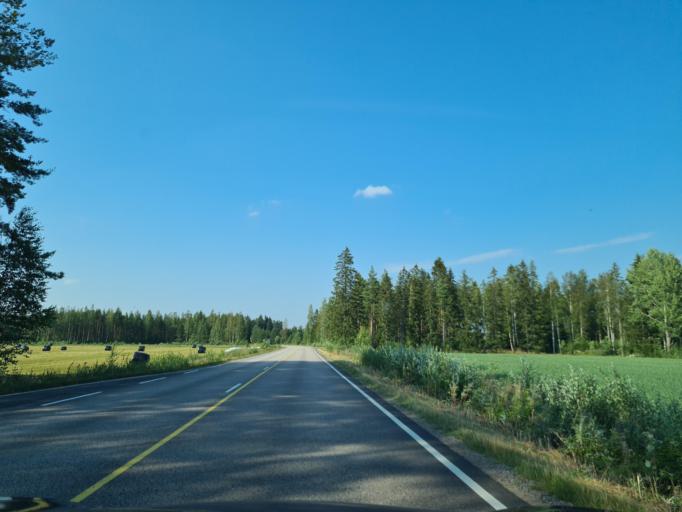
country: FI
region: Satakunta
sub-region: Pohjois-Satakunta
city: Karvia
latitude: 62.1889
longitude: 22.5966
